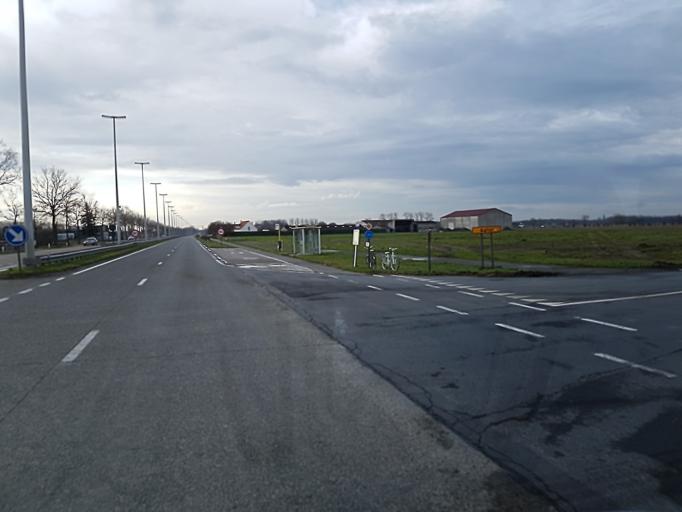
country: BE
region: Flanders
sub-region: Provincie Oost-Vlaanderen
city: Knesselare
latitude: 51.1220
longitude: 3.4261
